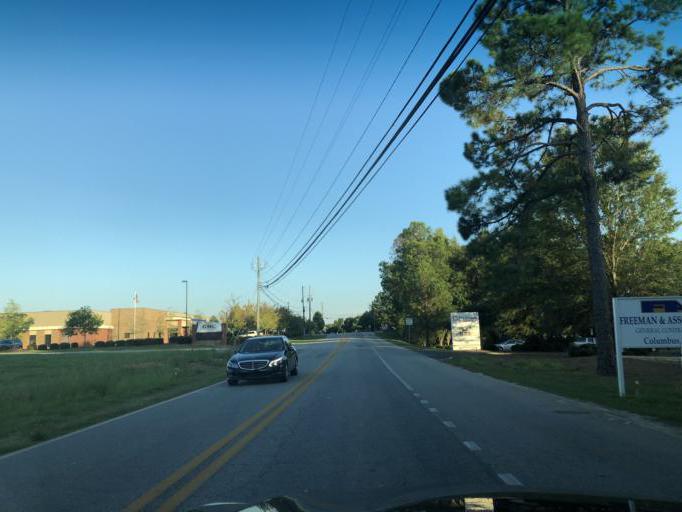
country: US
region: Georgia
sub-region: Muscogee County
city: Columbus
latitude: 32.5506
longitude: -84.8959
